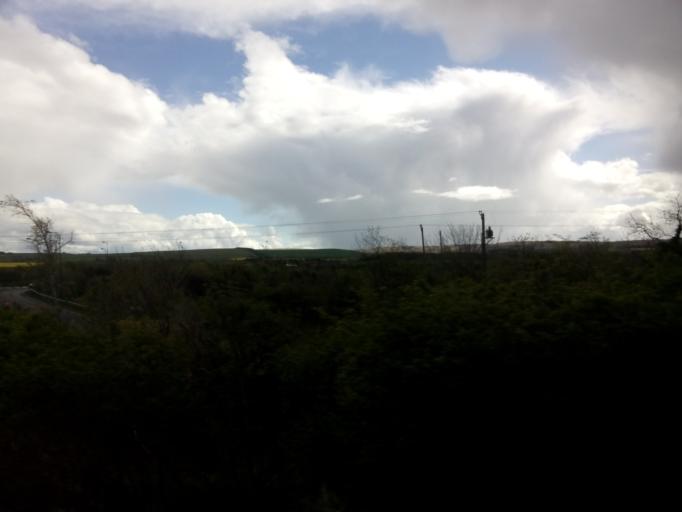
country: GB
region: Scotland
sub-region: East Lothian
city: Dunbar
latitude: 55.9898
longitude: -2.5643
